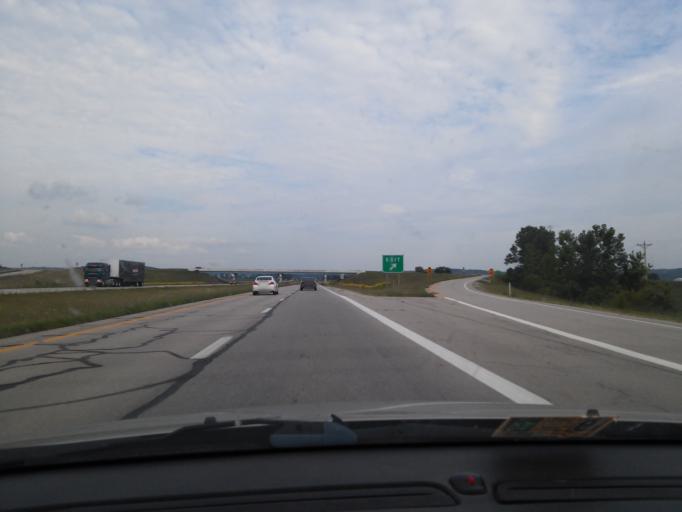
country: US
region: Ohio
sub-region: Ross County
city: Frankfort
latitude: 39.4286
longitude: -83.1694
